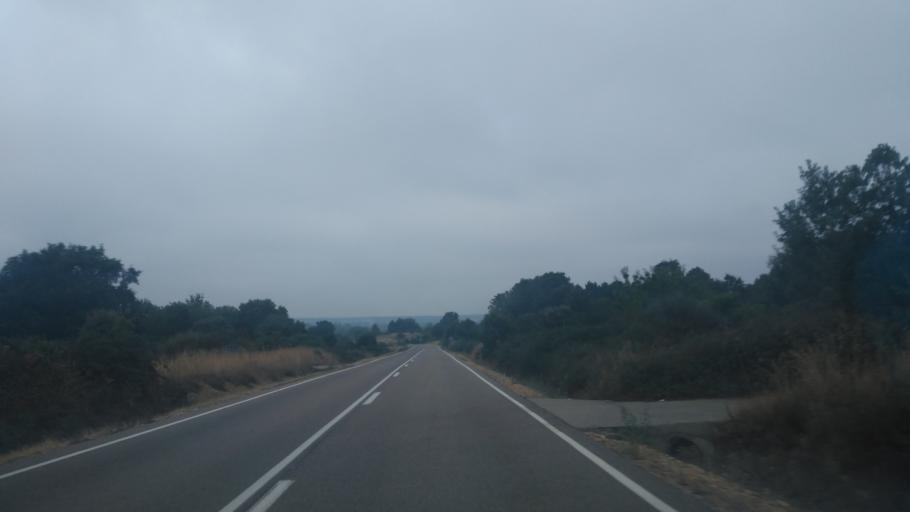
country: ES
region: Castille and Leon
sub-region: Provincia de Salamanca
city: Cereceda de la Sierra
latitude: 40.5609
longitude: -6.0804
